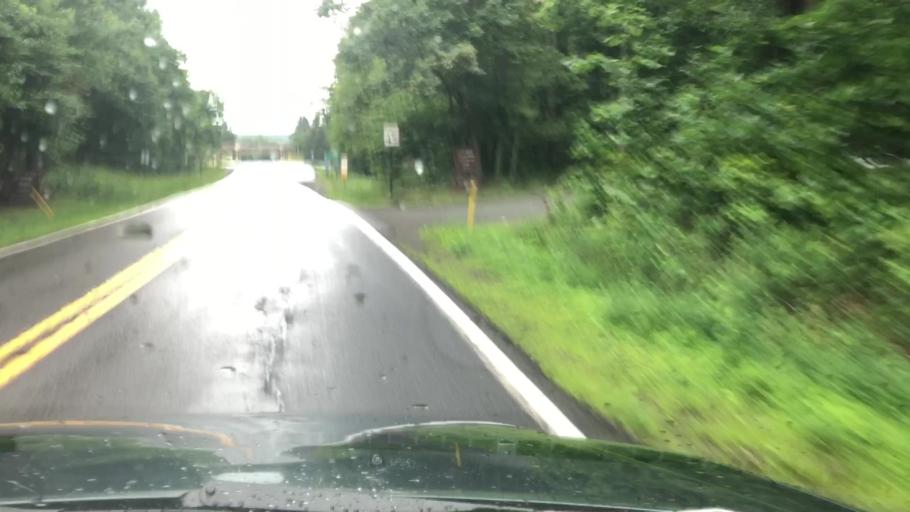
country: US
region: Pennsylvania
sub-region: Wayne County
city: Hawley
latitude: 41.3581
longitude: -75.2042
